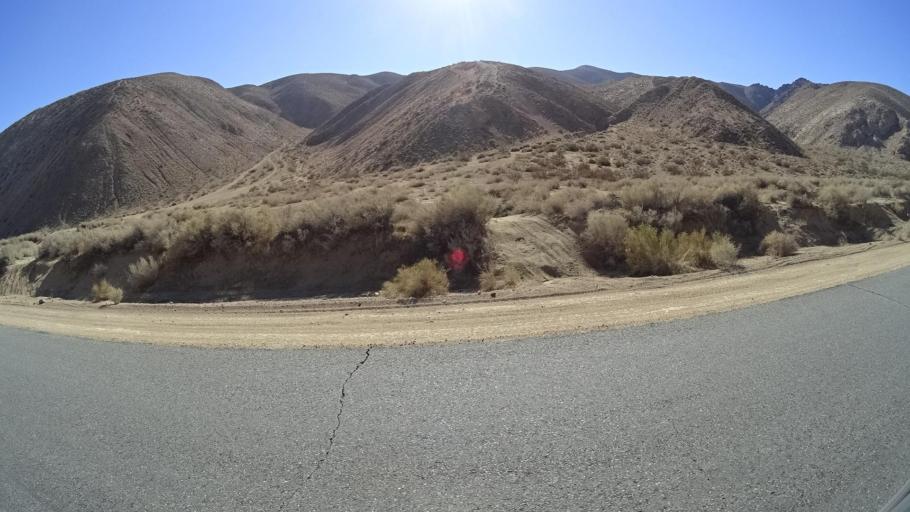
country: US
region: California
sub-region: Kern County
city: California City
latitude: 35.3141
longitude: -118.0592
